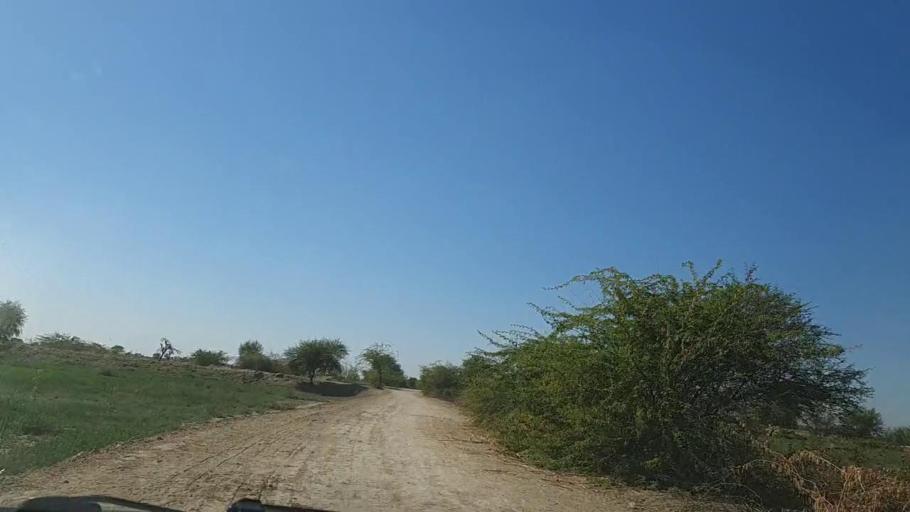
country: PK
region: Sindh
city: Pithoro
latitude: 25.5610
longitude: 69.4719
